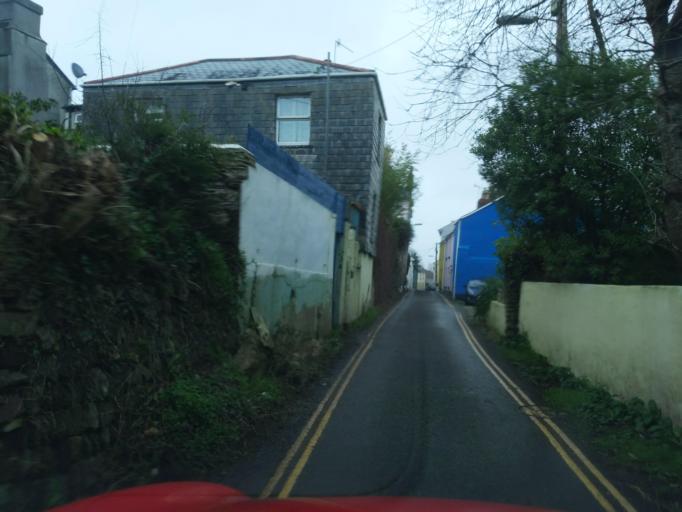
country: GB
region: England
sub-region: Cornwall
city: Torpoint
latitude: 50.3460
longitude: -4.2221
